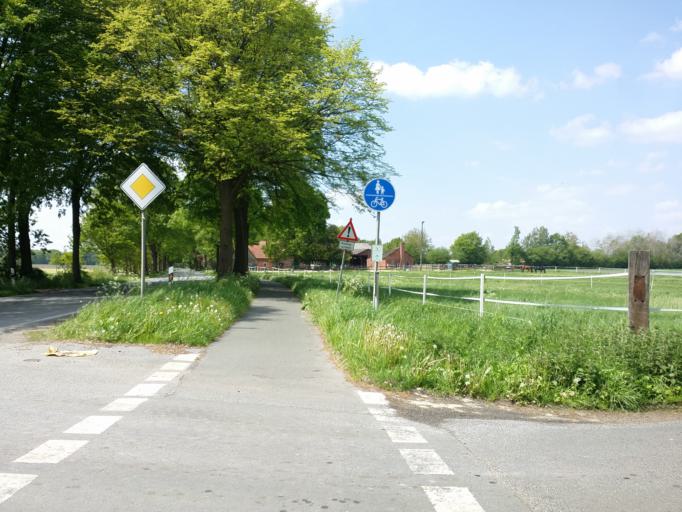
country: DE
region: Lower Saxony
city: Lubberstedt
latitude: 53.2988
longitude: 8.7713
